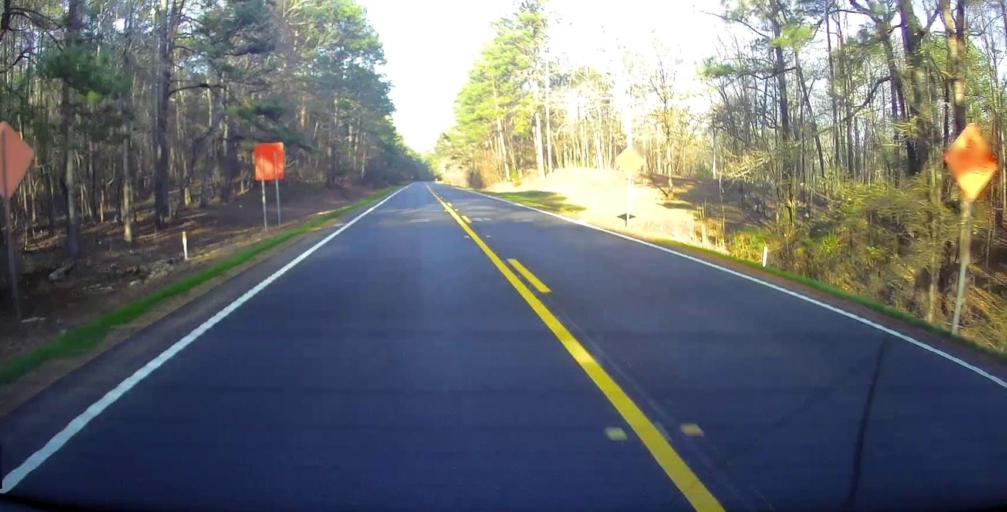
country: US
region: Georgia
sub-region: Harris County
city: Hamilton
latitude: 32.7462
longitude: -84.9412
